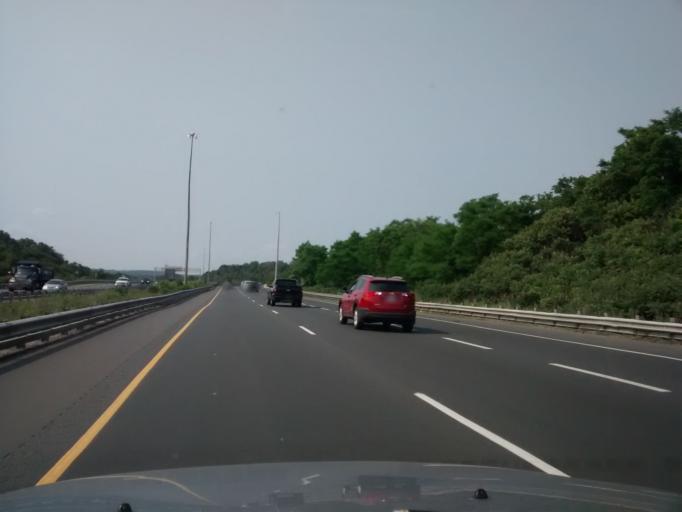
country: CA
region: Ontario
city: Hamilton
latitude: 43.2668
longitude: -79.8927
